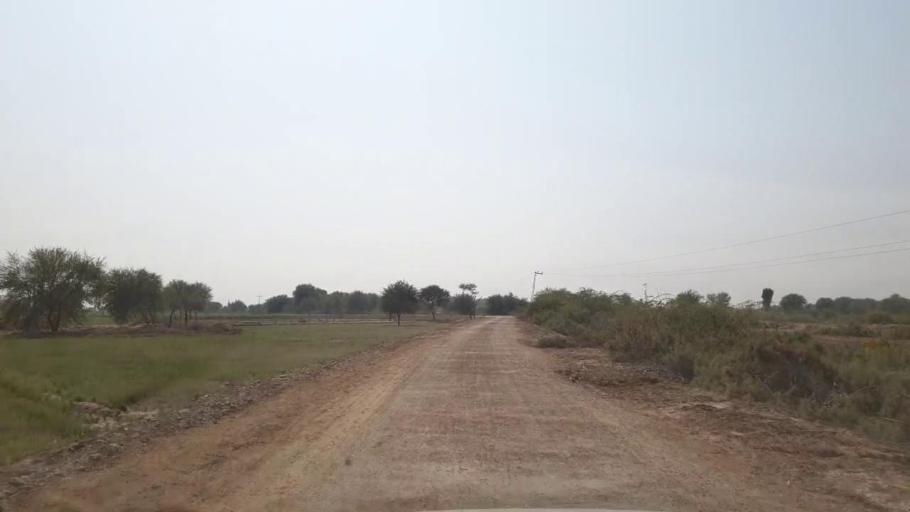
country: PK
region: Sindh
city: Mirpur Khas
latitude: 25.6318
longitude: 69.1433
